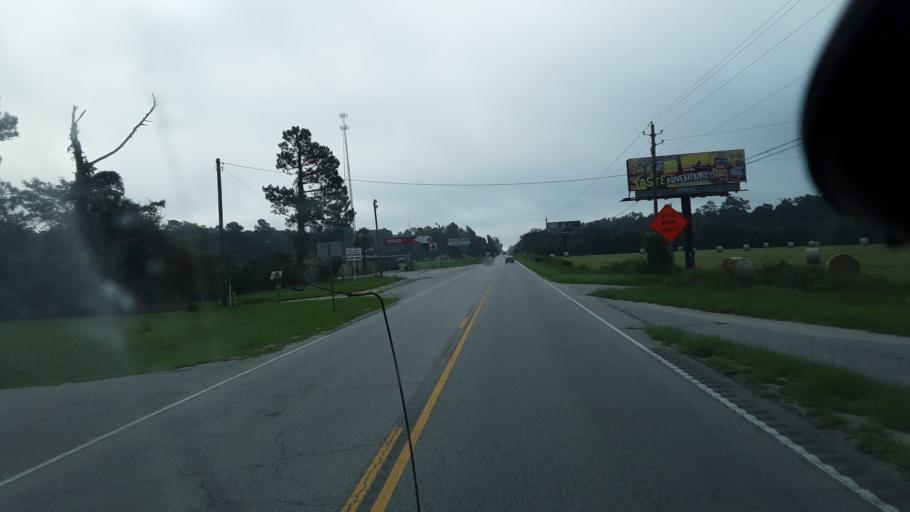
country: US
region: South Carolina
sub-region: Florence County
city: Johnsonville
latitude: 33.8665
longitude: -79.3353
